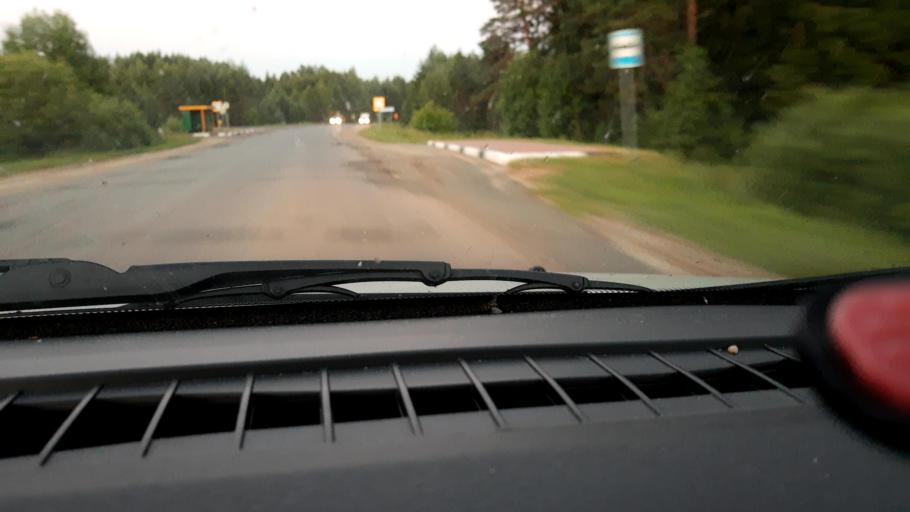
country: RU
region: Nizjnij Novgorod
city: Uren'
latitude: 57.4820
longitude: 46.0302
